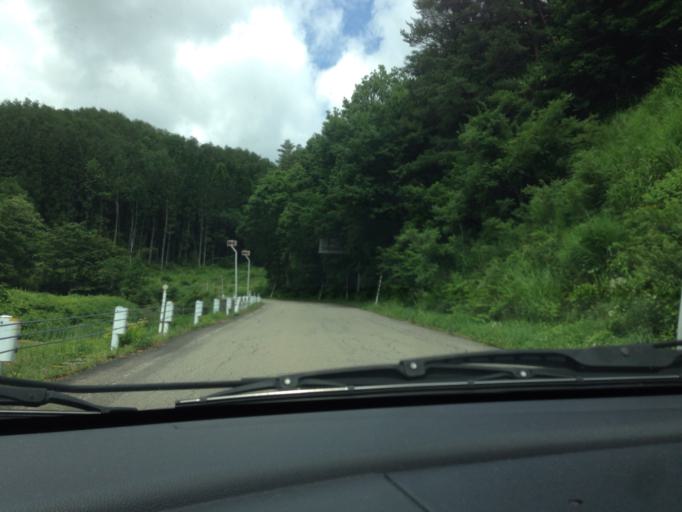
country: JP
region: Fukushima
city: Kitakata
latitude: 37.3249
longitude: 139.8602
